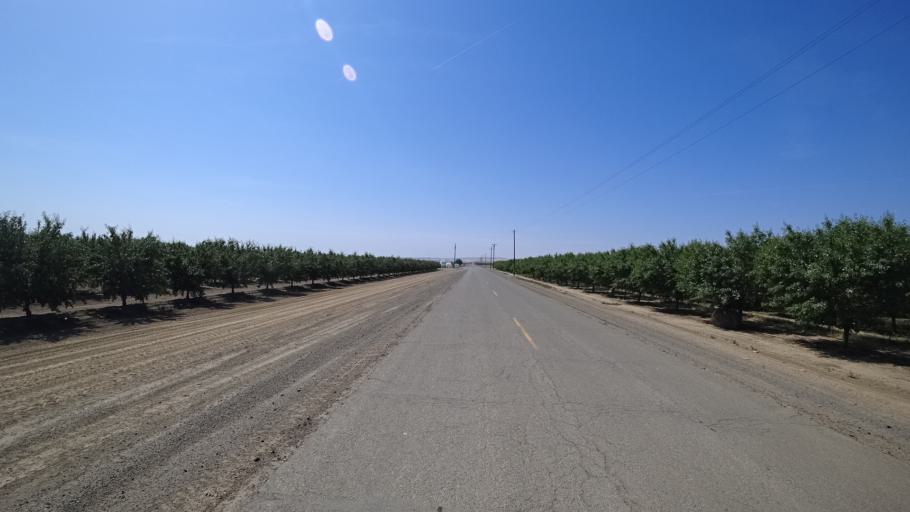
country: US
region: California
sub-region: Kings County
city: Kettleman City
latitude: 36.0815
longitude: -120.0037
